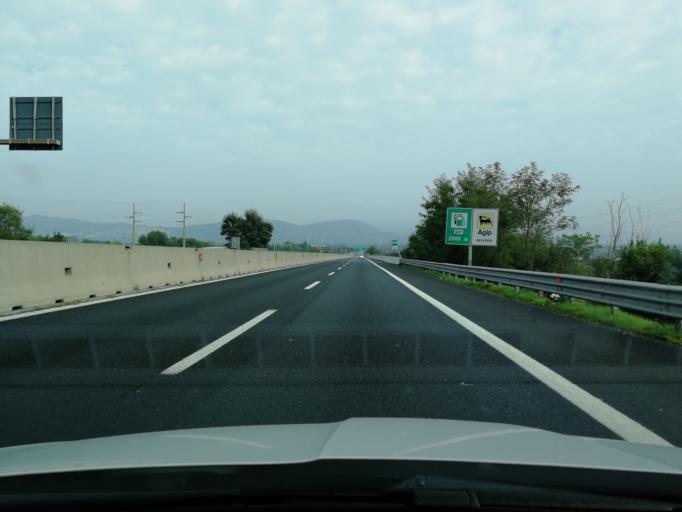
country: IT
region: Latium
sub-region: Citta metropolitana di Roma Capitale
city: Bagni di Tivoli
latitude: 41.9265
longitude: 12.7133
